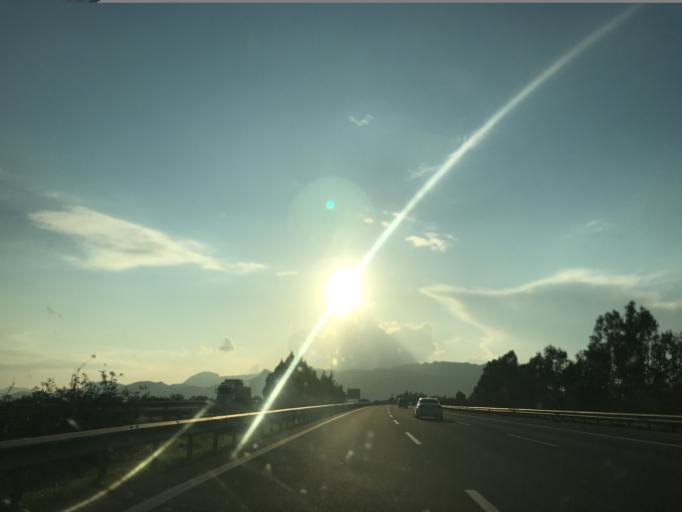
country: TR
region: Adana
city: Ceyhan
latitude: 36.9835
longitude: 35.7949
